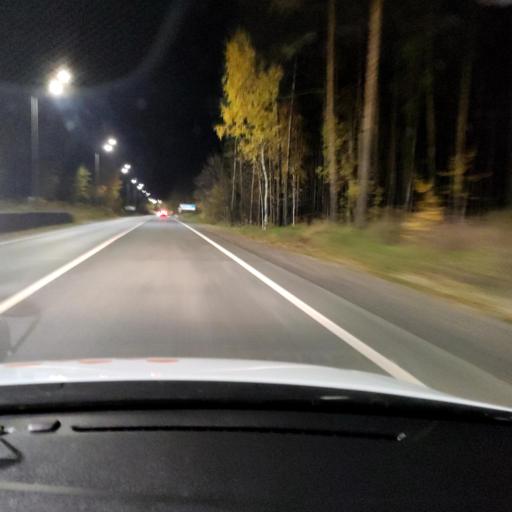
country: RU
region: Tatarstan
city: Verkhniy Uslon
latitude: 55.6393
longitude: 49.0326
